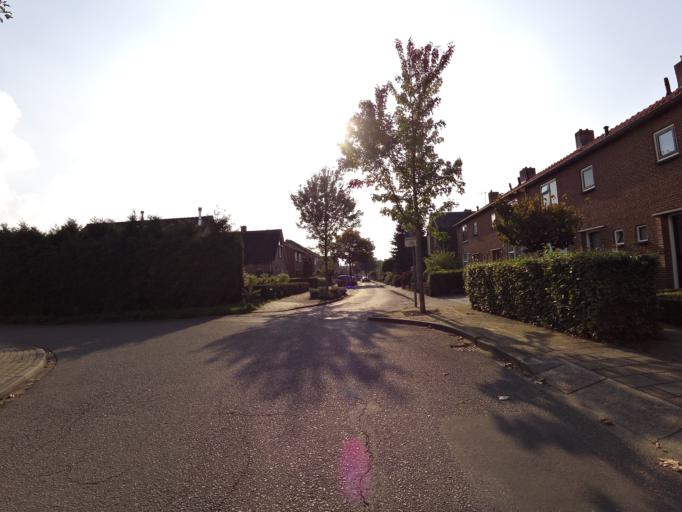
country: NL
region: Gelderland
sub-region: Gemeente Aalten
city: Aalten
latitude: 51.9193
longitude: 6.5860
